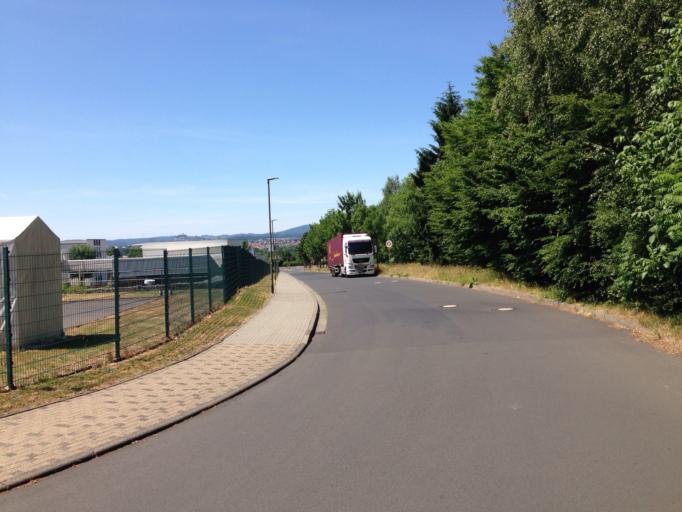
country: DE
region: Hesse
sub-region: Regierungsbezirk Giessen
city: Alten Buseck
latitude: 50.5932
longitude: 8.7398
